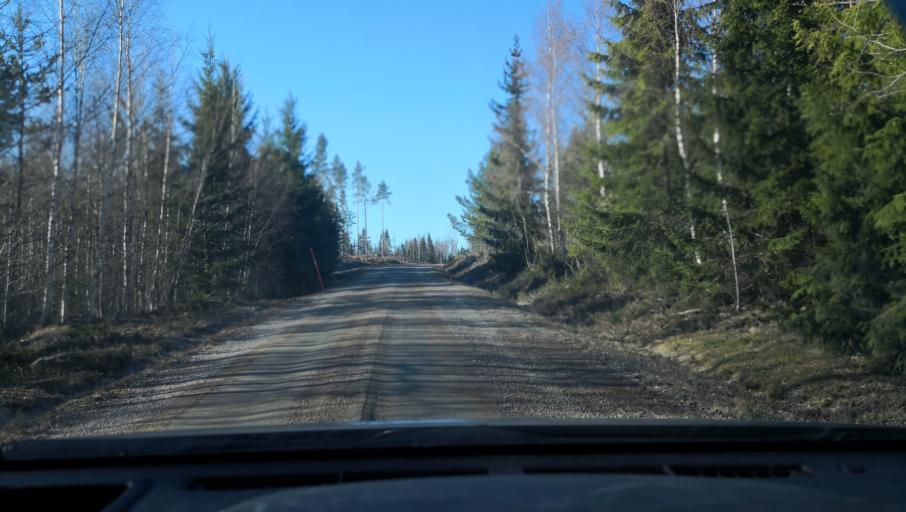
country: SE
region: Vaestmanland
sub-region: Sala Kommun
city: Sala
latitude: 60.1582
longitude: 16.6295
